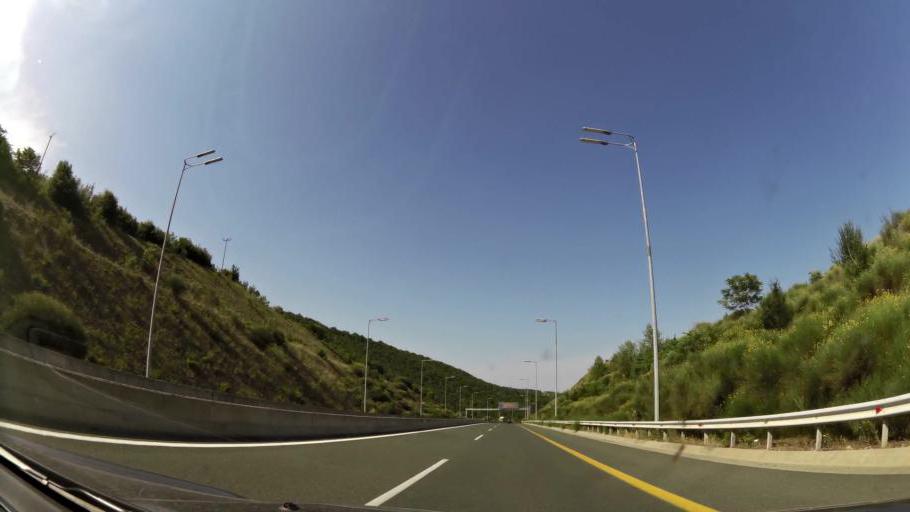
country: GR
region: Central Macedonia
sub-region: Nomos Imathias
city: Veroia
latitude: 40.4443
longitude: 22.1993
